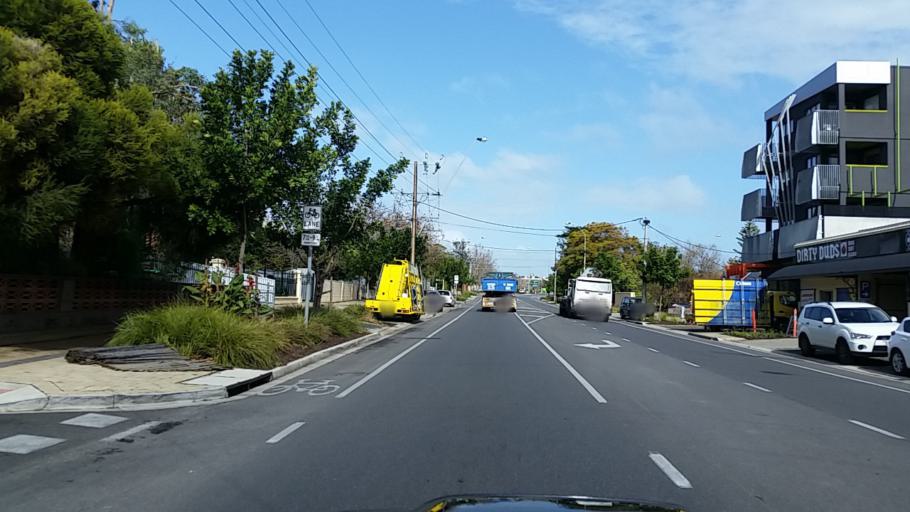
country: AU
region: South Australia
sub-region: Prospect
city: Prospect
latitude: -34.8937
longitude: 138.5855
